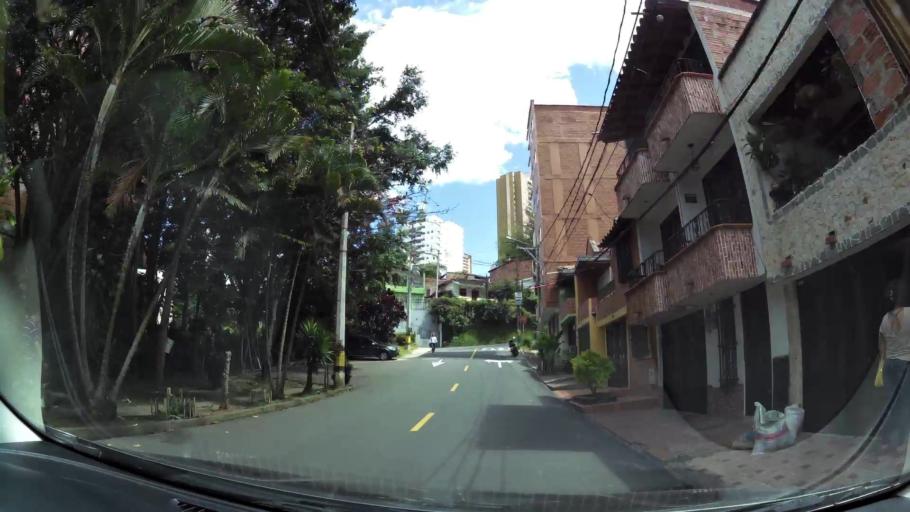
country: CO
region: Antioquia
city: Sabaneta
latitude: 6.1462
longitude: -75.6224
